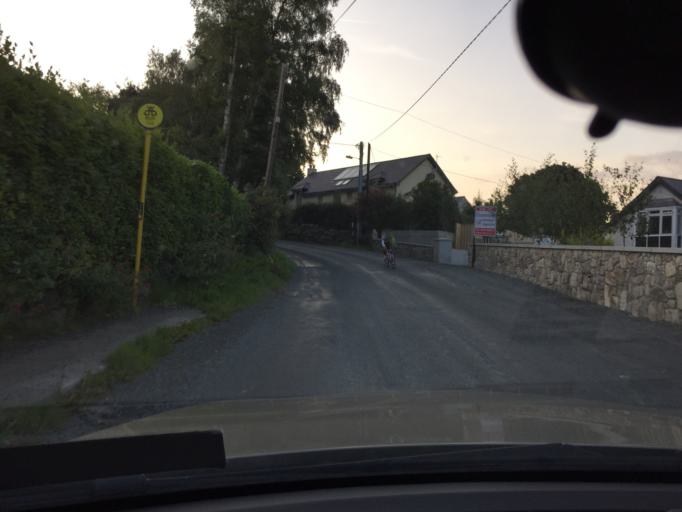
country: IE
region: Leinster
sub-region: Wicklow
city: Enniskerry
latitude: 53.1962
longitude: -6.1927
